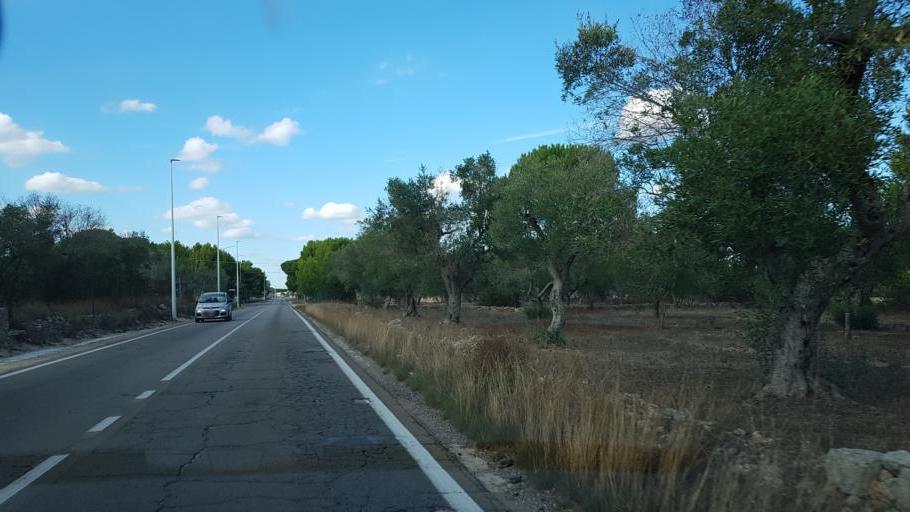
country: IT
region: Apulia
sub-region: Provincia di Lecce
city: Nardo
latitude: 40.1416
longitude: 18.0188
